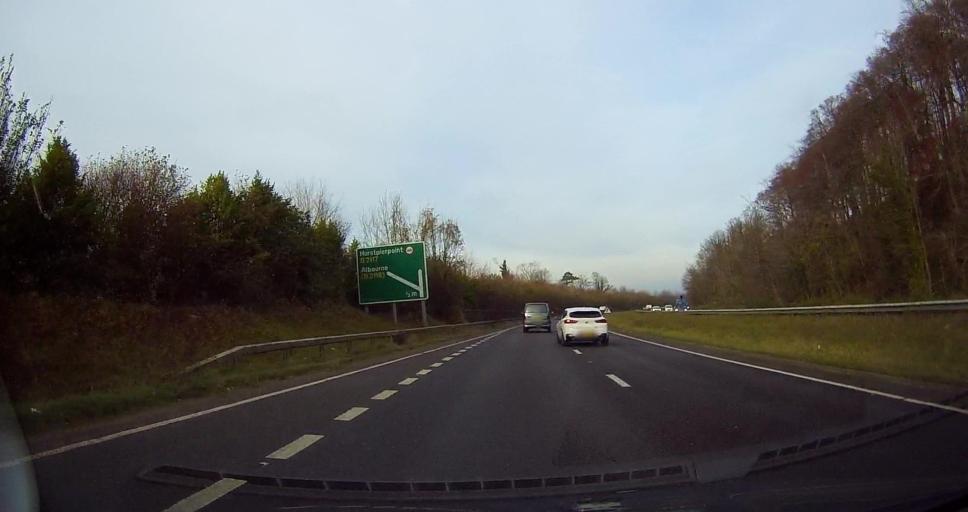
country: GB
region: England
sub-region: West Sussex
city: Hurstpierpoint
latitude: 50.9088
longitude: -0.1910
